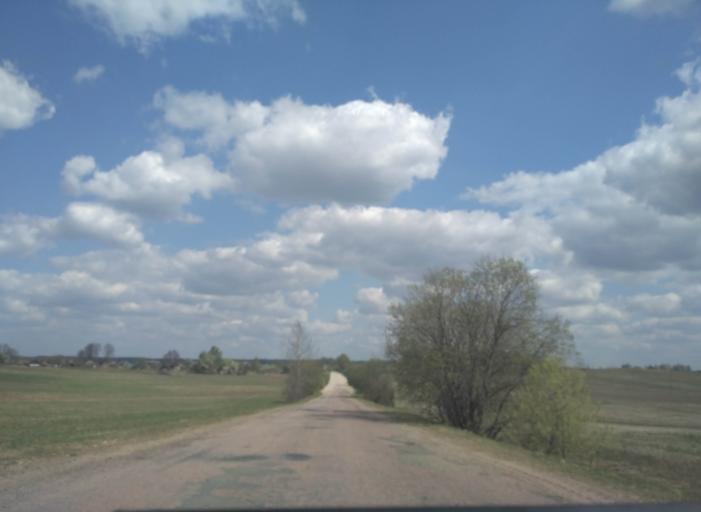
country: BY
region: Minsk
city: Radashkovichy
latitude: 54.2082
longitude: 27.2781
